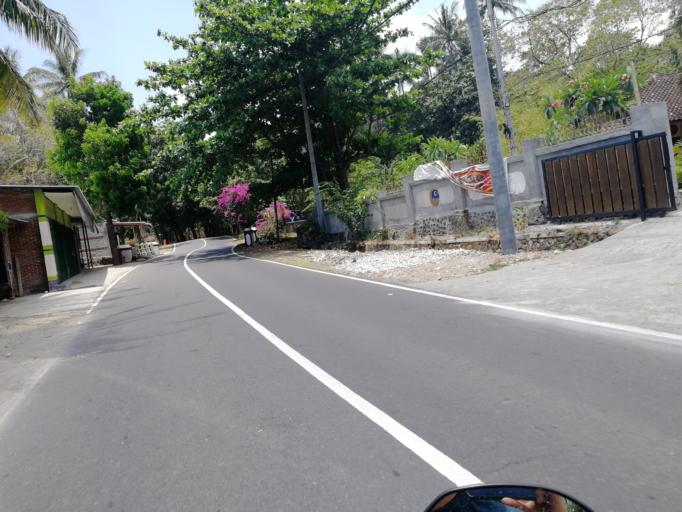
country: ID
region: West Nusa Tenggara
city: Karangsubagan
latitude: -8.4590
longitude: 116.0382
